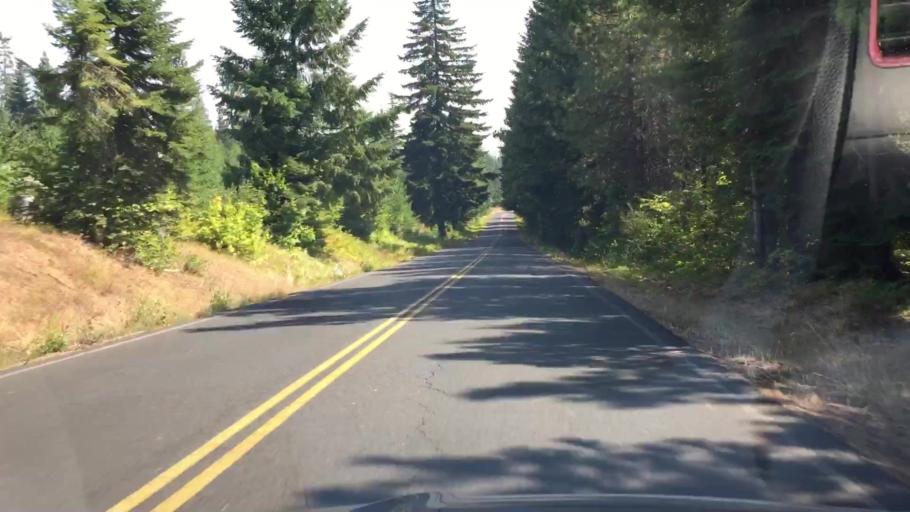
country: US
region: Washington
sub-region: Klickitat County
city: White Salmon
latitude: 46.0406
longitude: -121.5494
